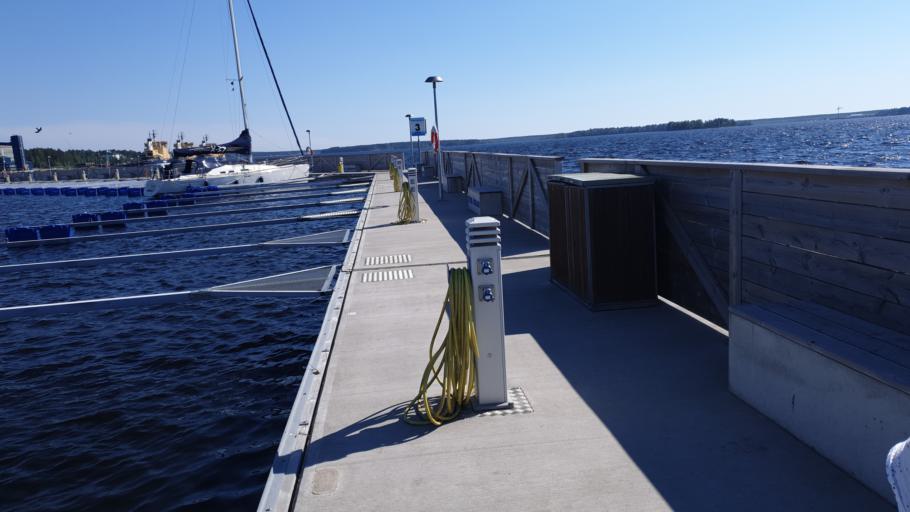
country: SE
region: Norrbotten
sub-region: Lulea Kommun
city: Lulea
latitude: 65.5791
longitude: 22.1607
